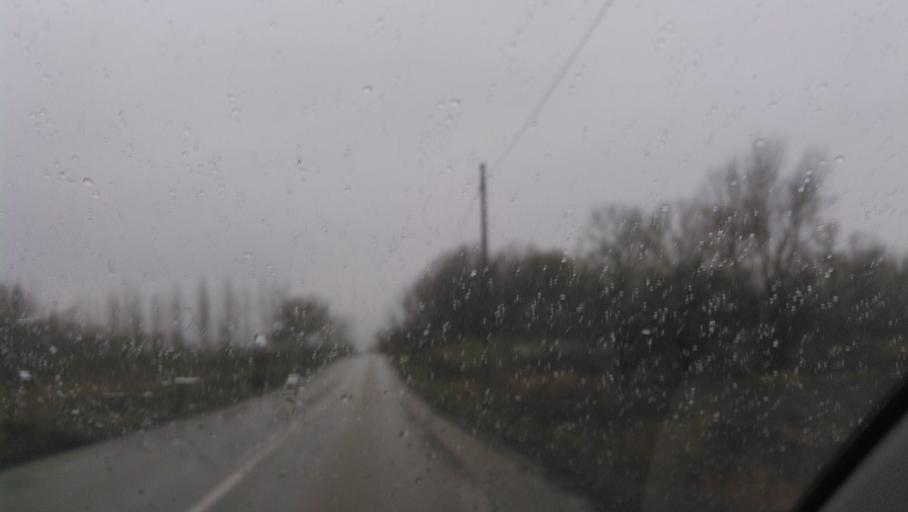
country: SK
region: Nitriansky
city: Kolarovo
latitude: 47.9335
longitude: 17.9869
